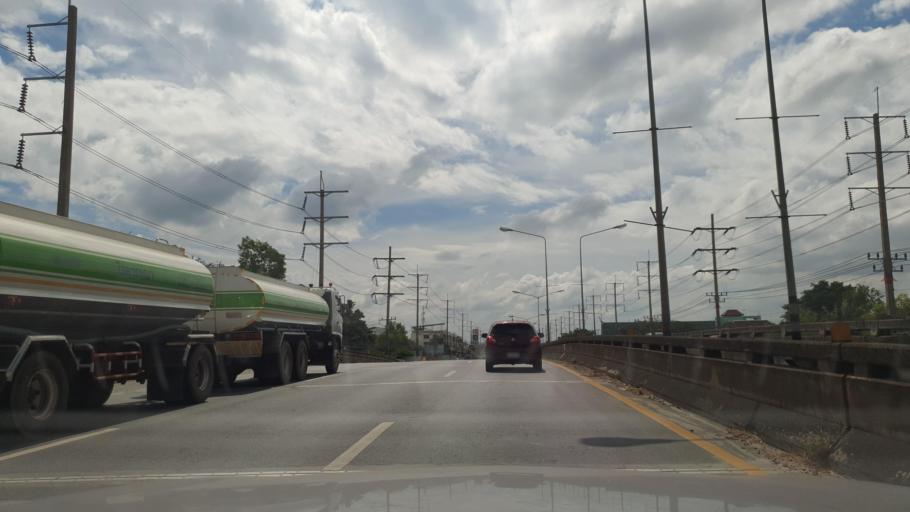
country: TH
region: Chachoengsao
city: Ban Pho
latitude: 13.6064
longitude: 101.0226
